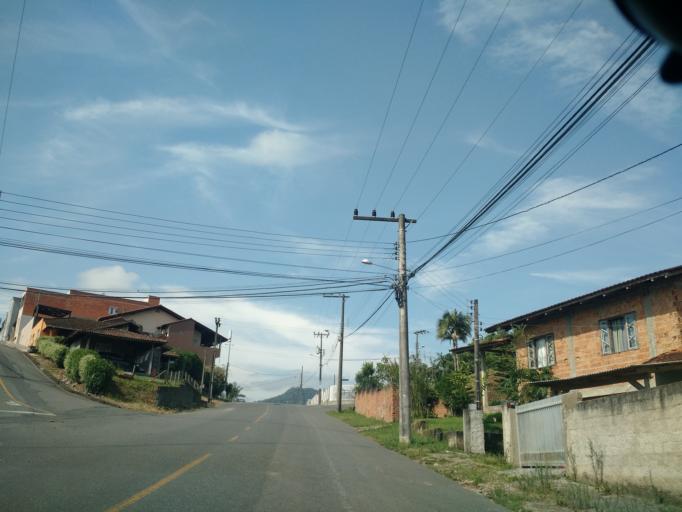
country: BR
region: Santa Catarina
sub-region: Jaragua Do Sul
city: Jaragua do Sul
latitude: -26.4925
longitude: -49.1016
